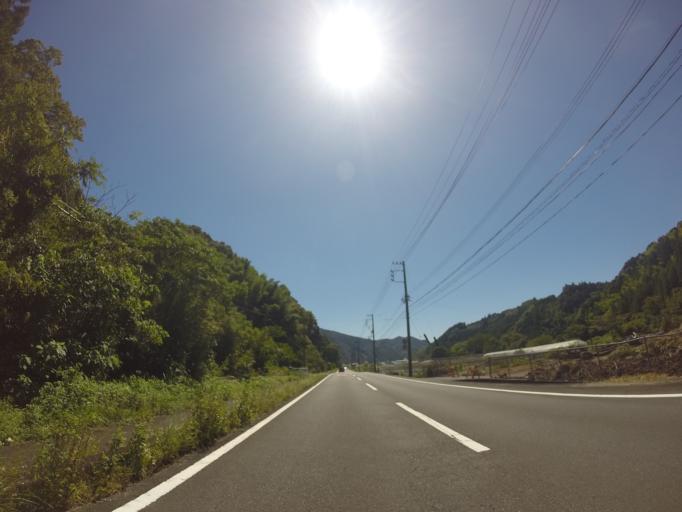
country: JP
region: Shizuoka
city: Fujieda
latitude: 34.9313
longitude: 138.2040
